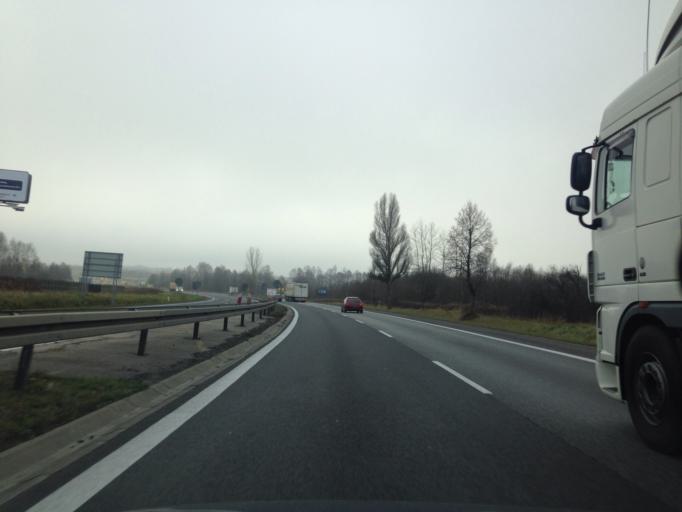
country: PL
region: Silesian Voivodeship
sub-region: Powiat myszkowski
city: Kozieglowy
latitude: 50.5954
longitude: 19.1503
